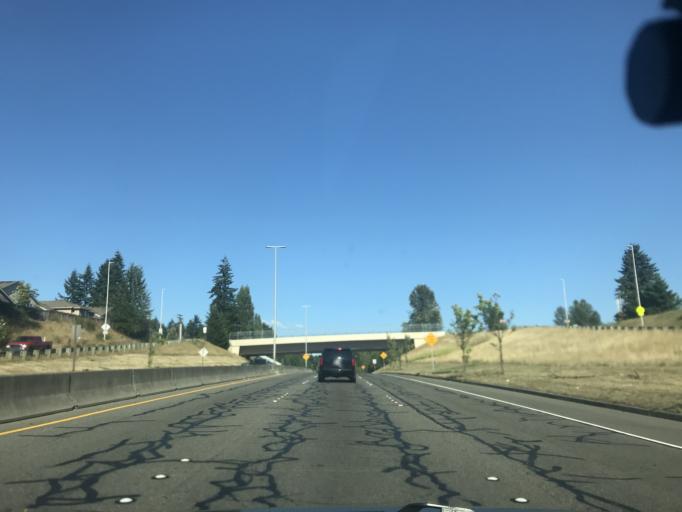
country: US
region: Washington
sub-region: King County
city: Lea Hill
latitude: 47.3558
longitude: -122.1989
